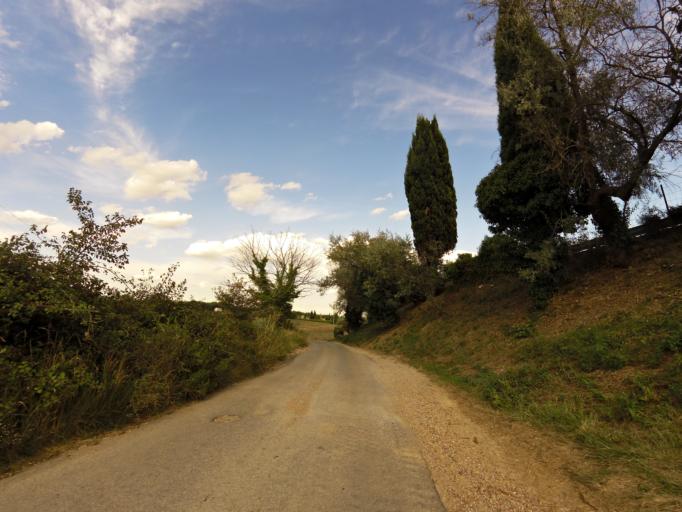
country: FR
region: Languedoc-Roussillon
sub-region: Departement du Gard
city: Aigues-Vives
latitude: 43.7279
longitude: 4.1792
